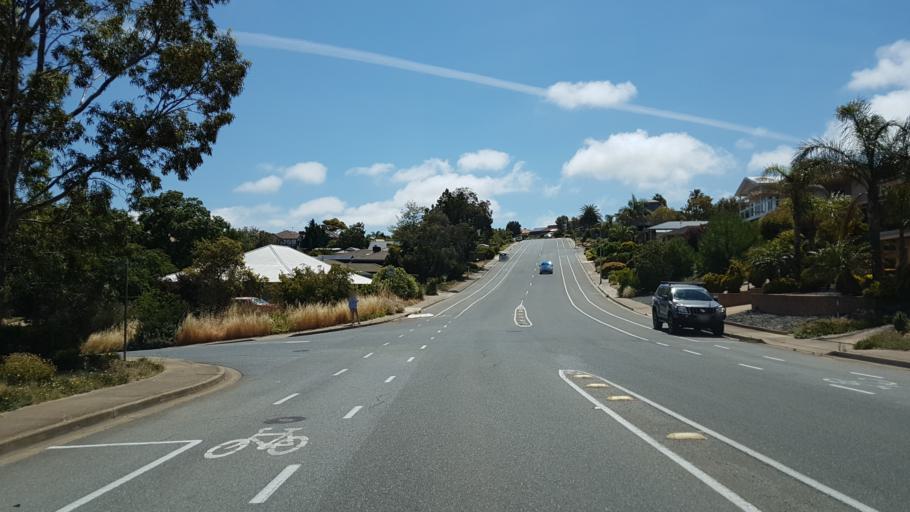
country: AU
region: South Australia
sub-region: Marion
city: Marino
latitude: -35.0657
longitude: 138.5087
